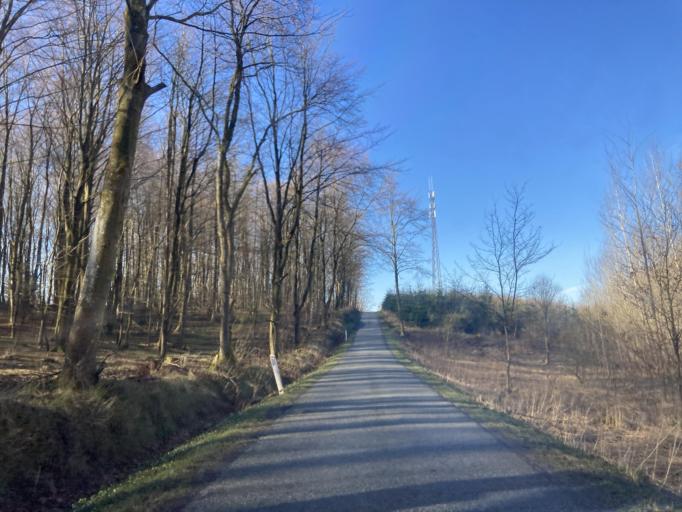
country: DK
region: Zealand
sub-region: Ringsted Kommune
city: Ringsted
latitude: 55.5013
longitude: 11.8429
